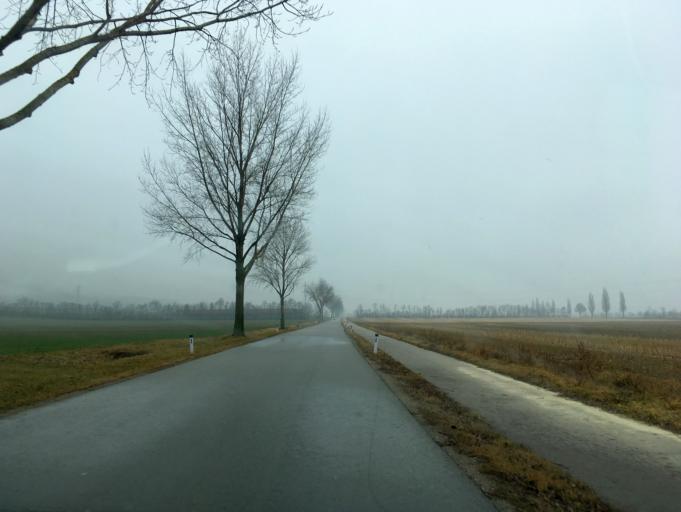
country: AT
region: Lower Austria
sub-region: Politischer Bezirk Bruck an der Leitha
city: Trautmannsdorf an der Leitha
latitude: 48.0512
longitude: 16.6514
